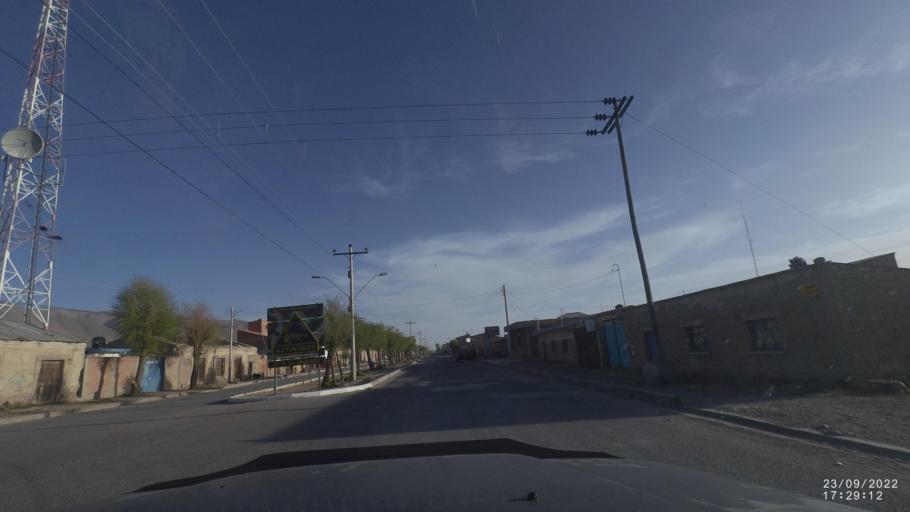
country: BO
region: Oruro
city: Challapata
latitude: -18.9010
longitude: -66.7769
